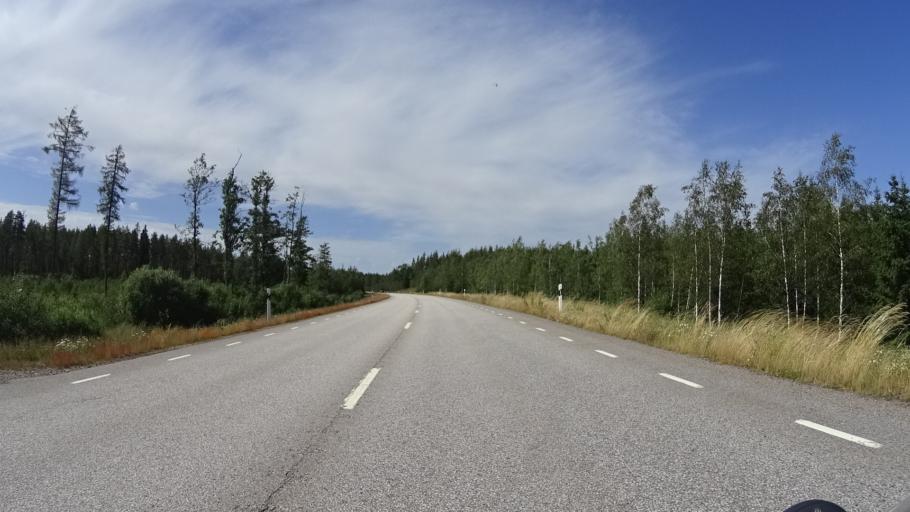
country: SE
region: Kalmar
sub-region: Vasterviks Kommun
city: Gamleby
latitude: 57.9536
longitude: 16.3771
